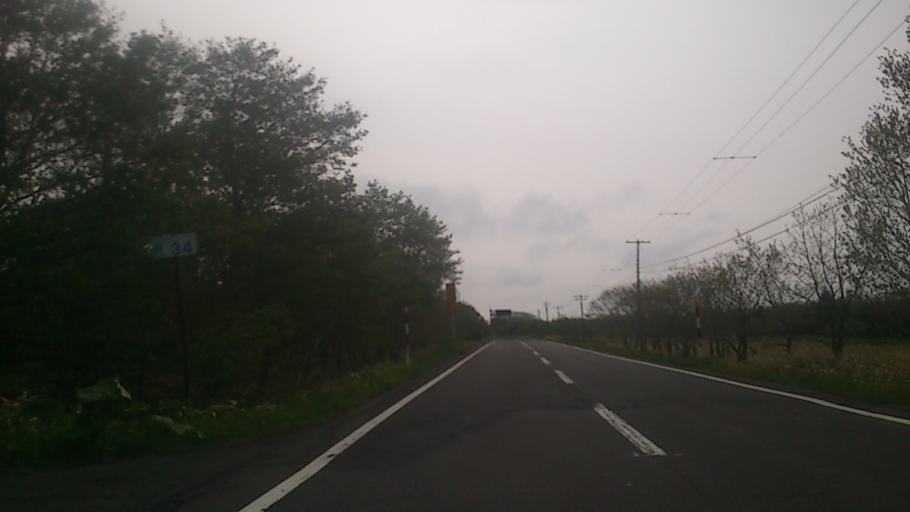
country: JP
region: Hokkaido
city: Nemuro
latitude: 43.2076
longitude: 145.3322
